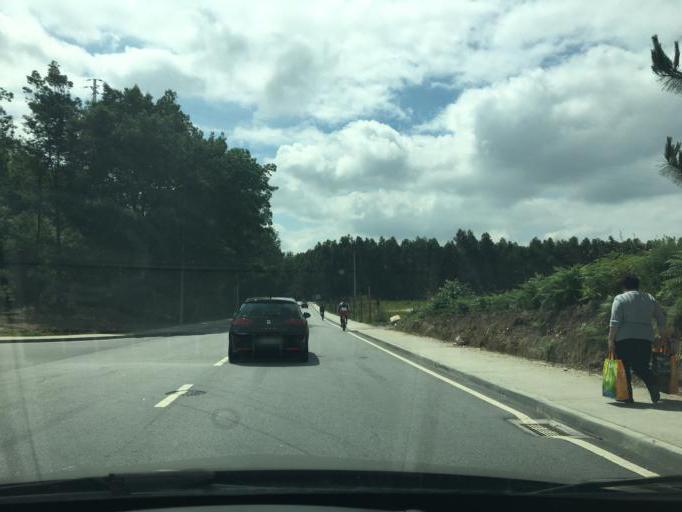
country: PT
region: Porto
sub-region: Maia
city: Gemunde
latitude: 41.2562
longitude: -8.6433
